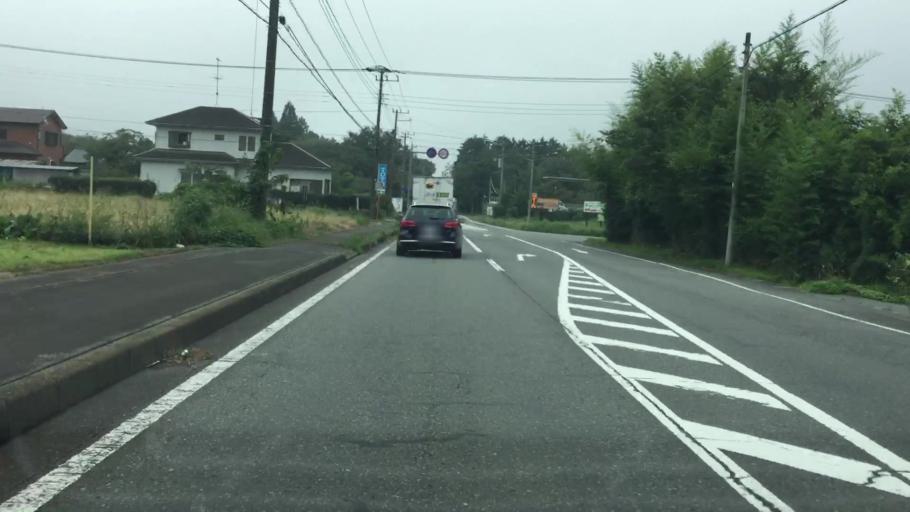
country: JP
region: Shizuoka
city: Fujinomiya
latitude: 35.3364
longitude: 138.5944
